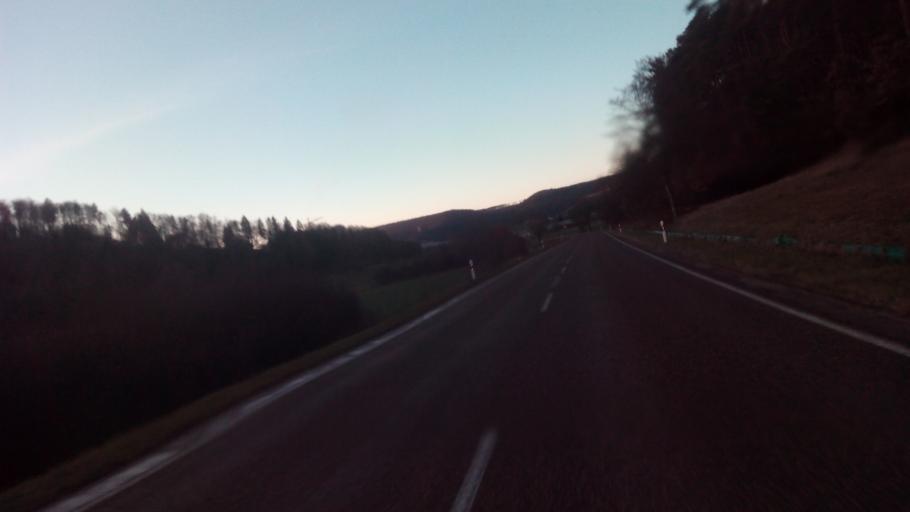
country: DE
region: Baden-Wuerttemberg
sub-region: Tuebingen Region
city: Schelklingen
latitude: 48.3588
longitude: 9.7457
